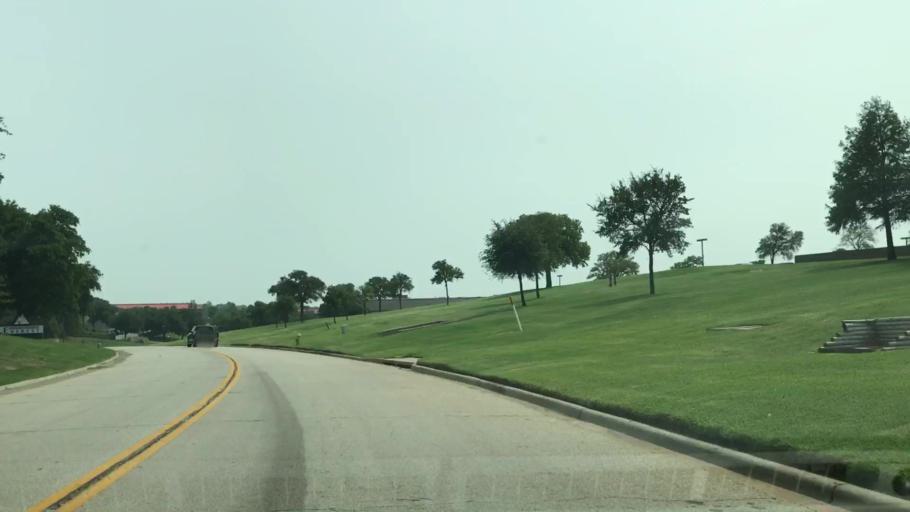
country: US
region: Texas
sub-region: Dallas County
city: Irving
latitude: 32.8706
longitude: -96.9749
